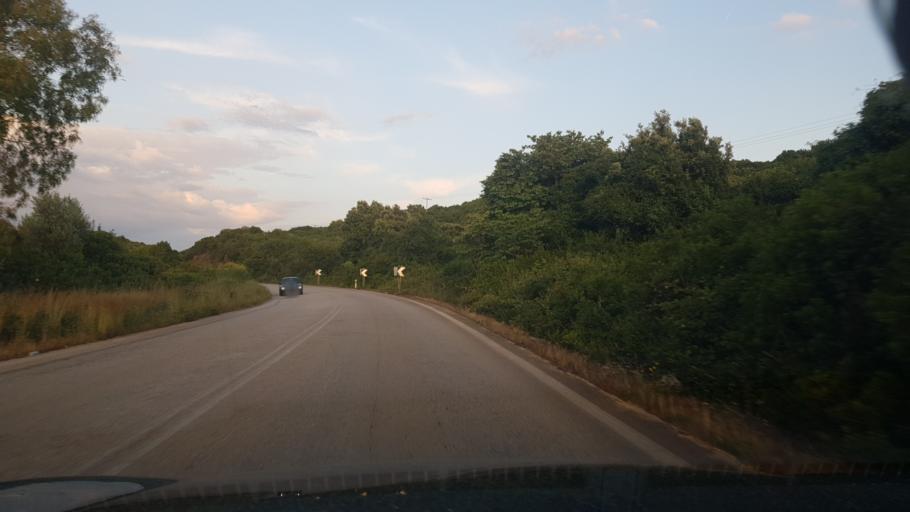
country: GR
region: Ionian Islands
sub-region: Lefkada
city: Lefkada
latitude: 38.8638
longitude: 20.7781
